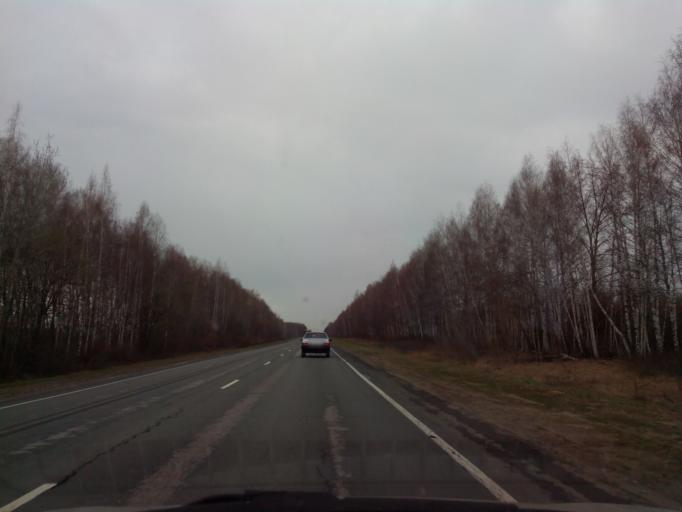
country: RU
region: Tambov
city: Michurinsk
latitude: 53.0661
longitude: 40.4399
